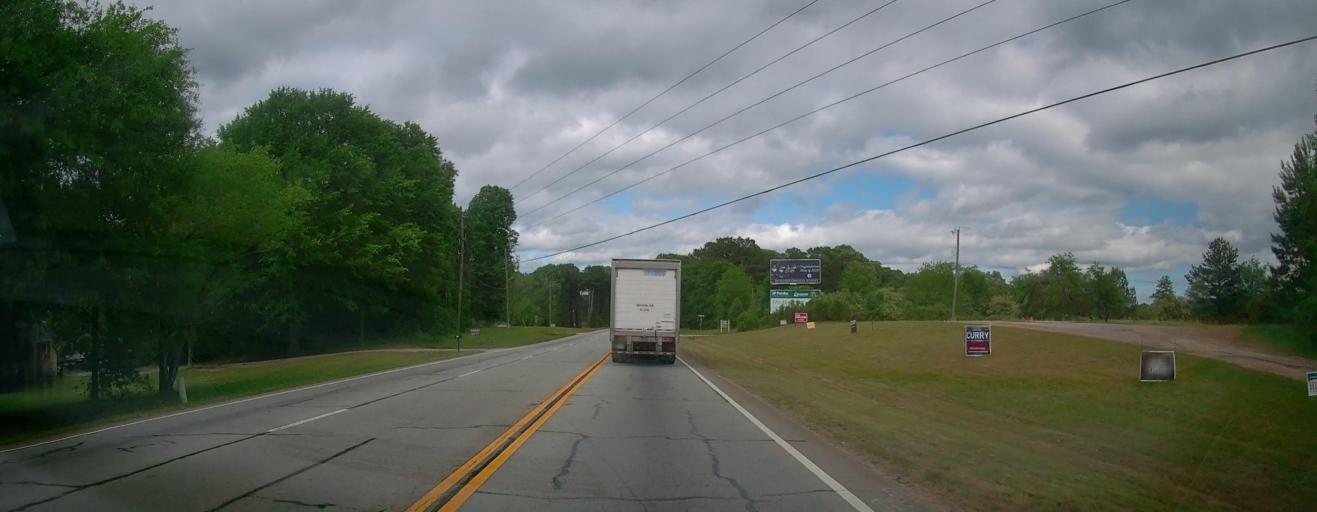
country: US
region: Georgia
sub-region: Walton County
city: Monroe
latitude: 33.7843
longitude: -83.7630
